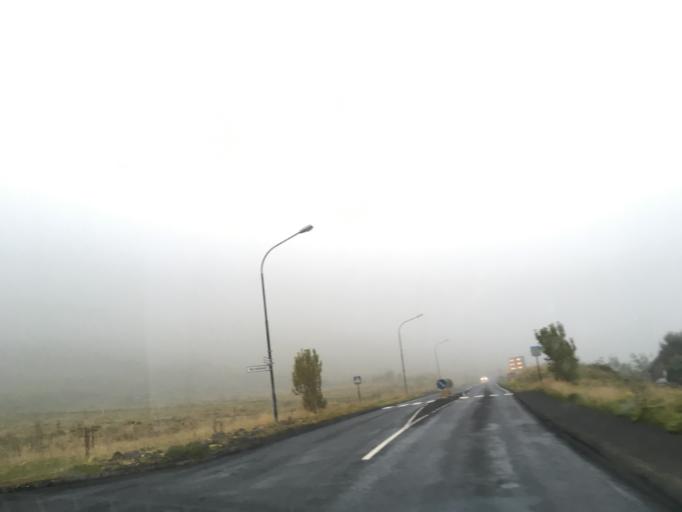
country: IS
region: South
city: Vestmannaeyjar
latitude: 63.4212
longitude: -19.0120
